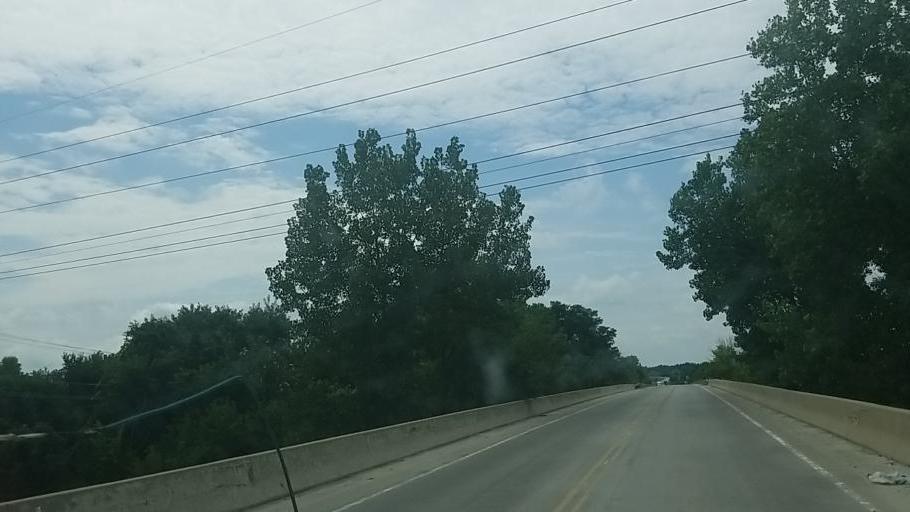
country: US
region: Ohio
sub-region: Franklin County
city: Obetz
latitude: 39.8313
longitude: -82.9544
